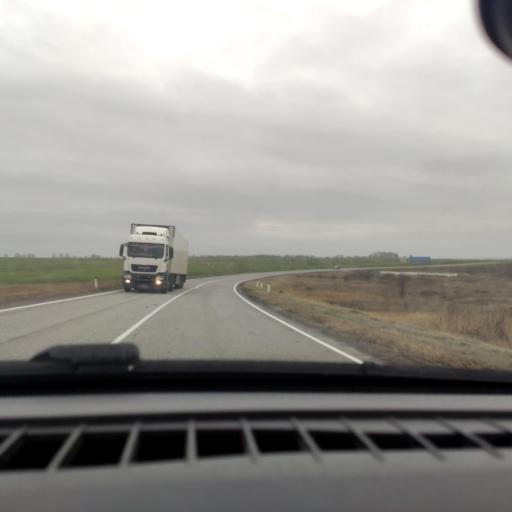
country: RU
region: Belgorod
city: Alekseyevka
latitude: 50.7743
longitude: 38.8394
